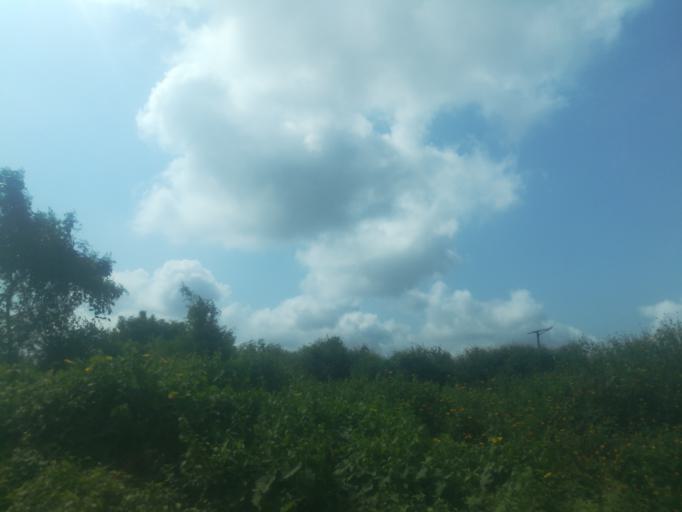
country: NG
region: Oyo
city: Moniya
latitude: 7.5377
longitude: 3.9165
